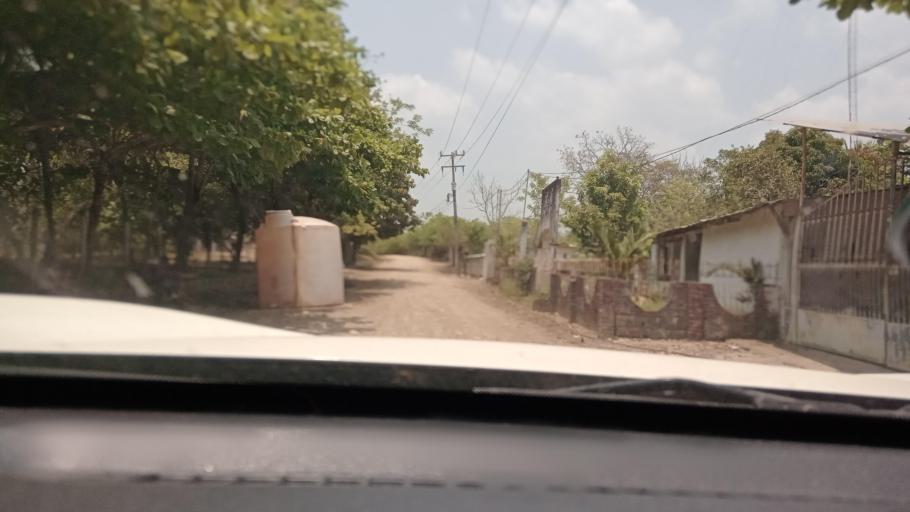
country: MX
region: Tabasco
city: Chontalpa
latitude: 17.5655
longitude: -93.7130
